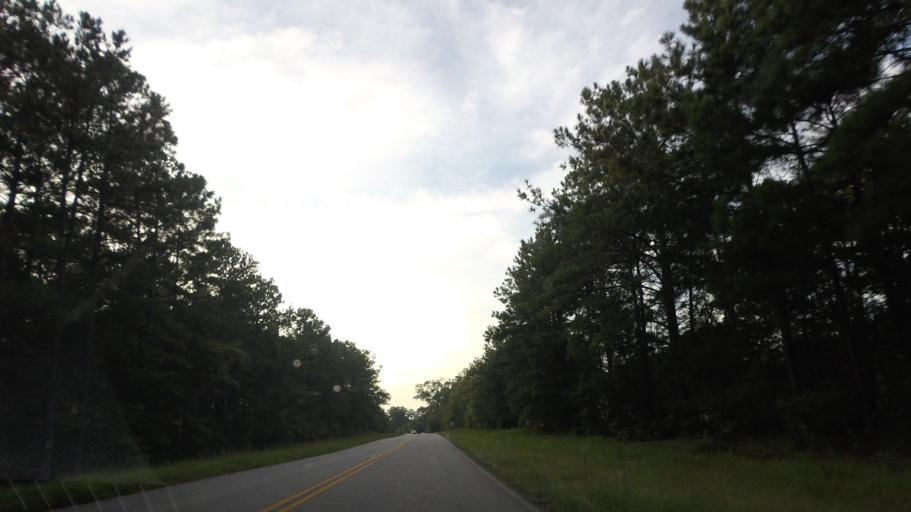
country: US
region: Georgia
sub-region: Bibb County
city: Macon
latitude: 32.8729
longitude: -83.5445
